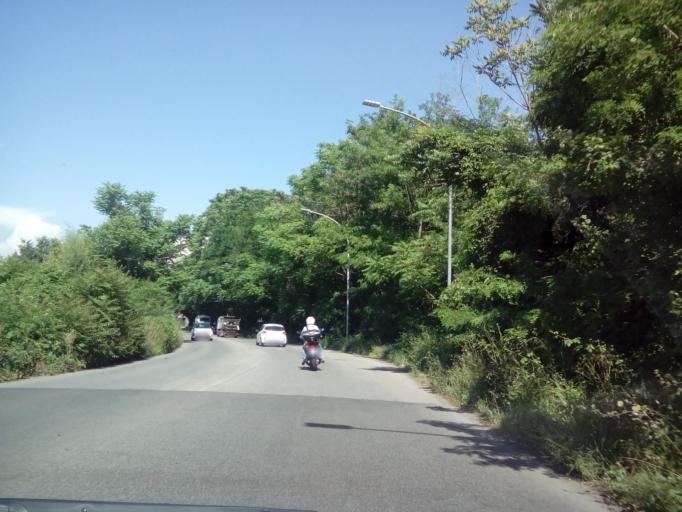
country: VA
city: Vatican City
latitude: 41.8455
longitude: 12.4713
